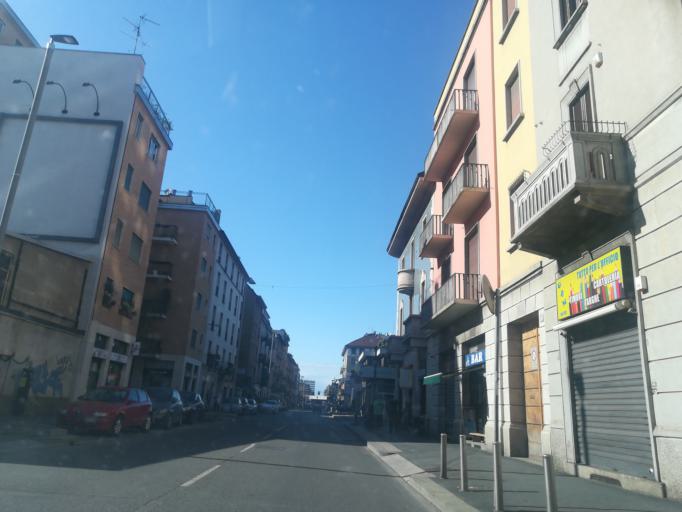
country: IT
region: Lombardy
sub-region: Citta metropolitana di Milano
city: Bresso
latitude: 45.5033
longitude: 9.1811
